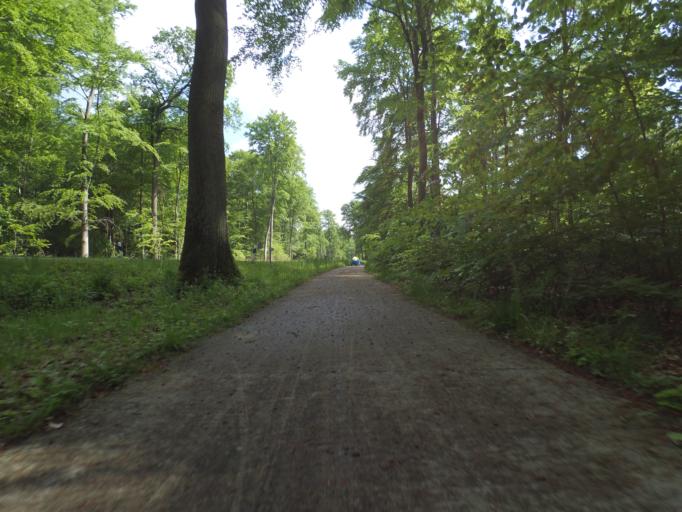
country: DE
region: Lower Saxony
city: Wendeburg
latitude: 52.3625
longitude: 10.3360
